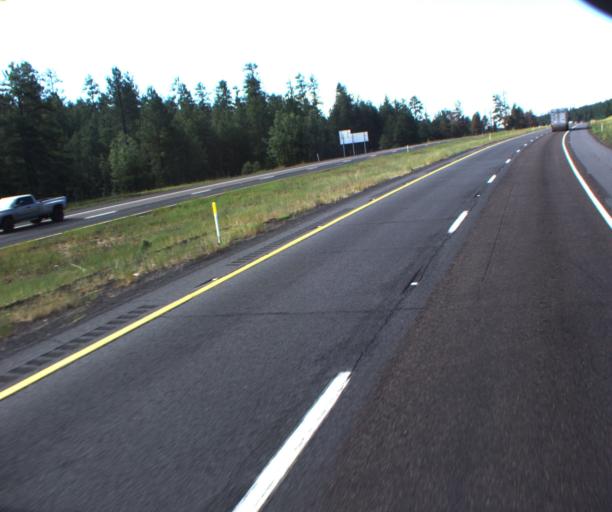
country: US
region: Arizona
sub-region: Coconino County
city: Mountainaire
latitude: 35.0332
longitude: -111.6841
